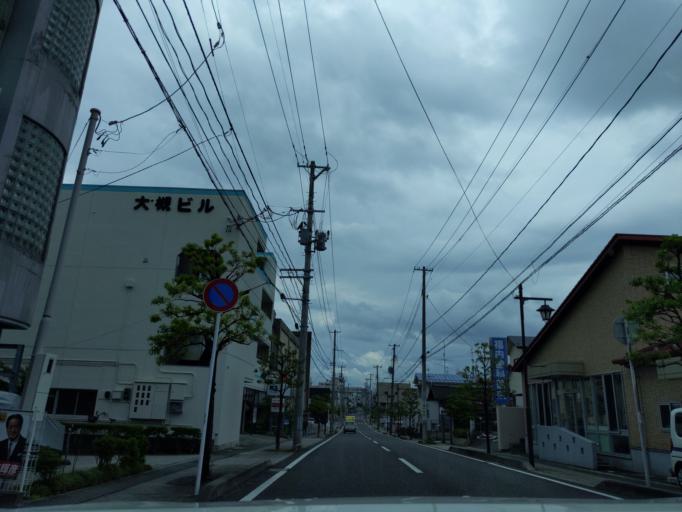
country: JP
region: Fukushima
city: Koriyama
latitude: 37.3906
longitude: 140.3719
